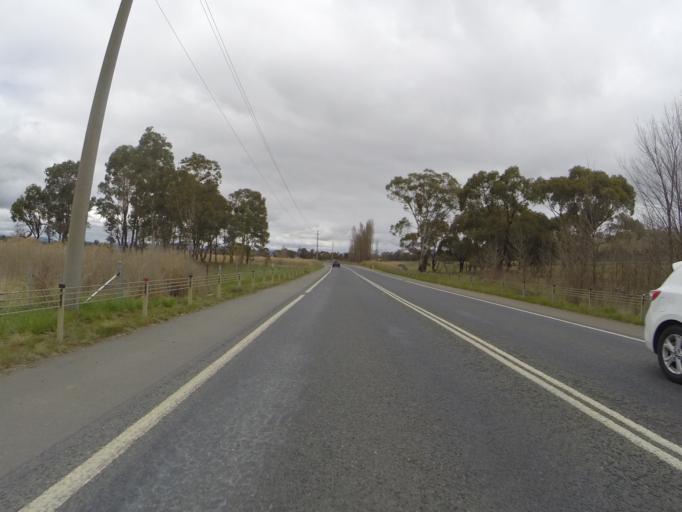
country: AU
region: Australian Capital Territory
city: Canberra
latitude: -35.2498
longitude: 149.1901
